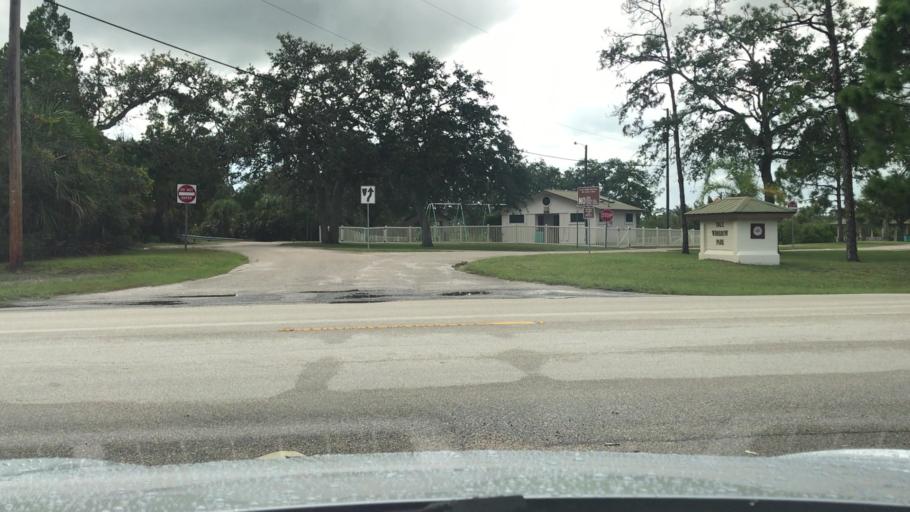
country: US
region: Florida
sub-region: Indian River County
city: Roseland
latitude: 27.8100
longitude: -80.5033
